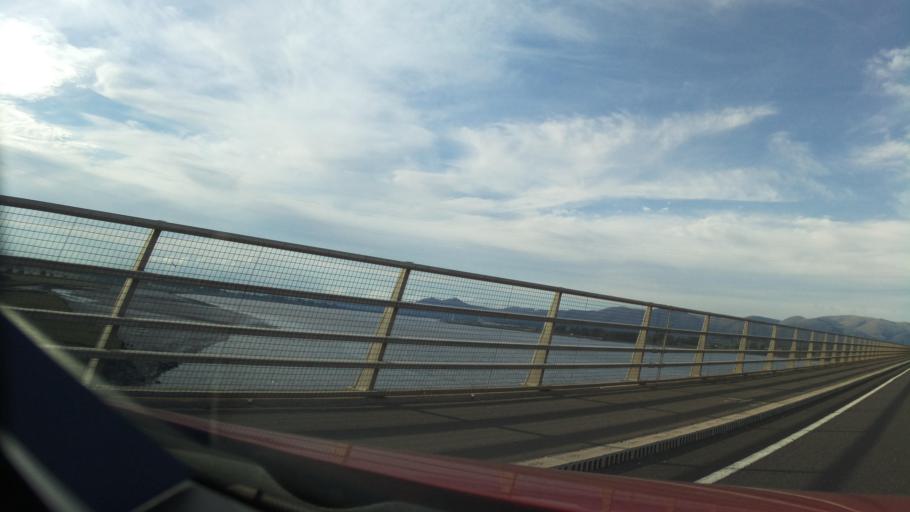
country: GB
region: Scotland
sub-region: Fife
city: Kincardine
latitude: 56.0647
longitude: -3.7335
